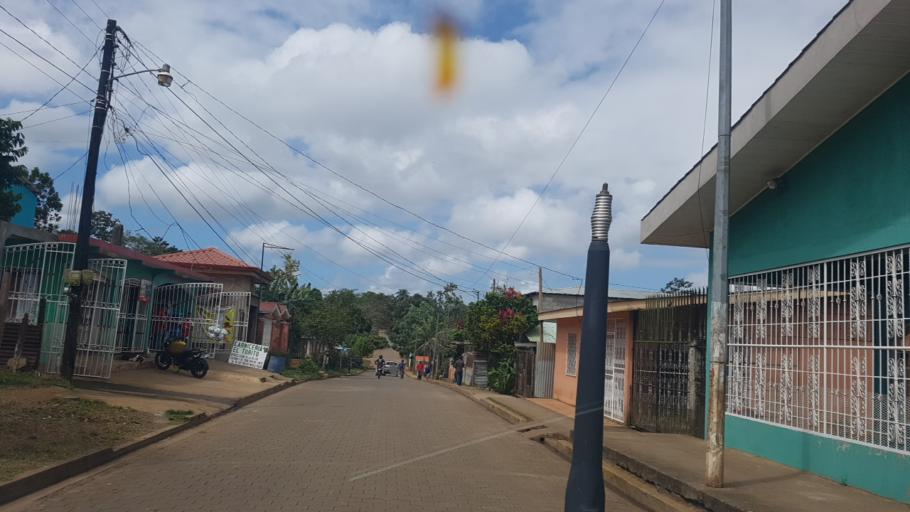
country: NI
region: Atlantico Sur
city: Nueva Guinea
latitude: 11.6889
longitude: -84.4588
